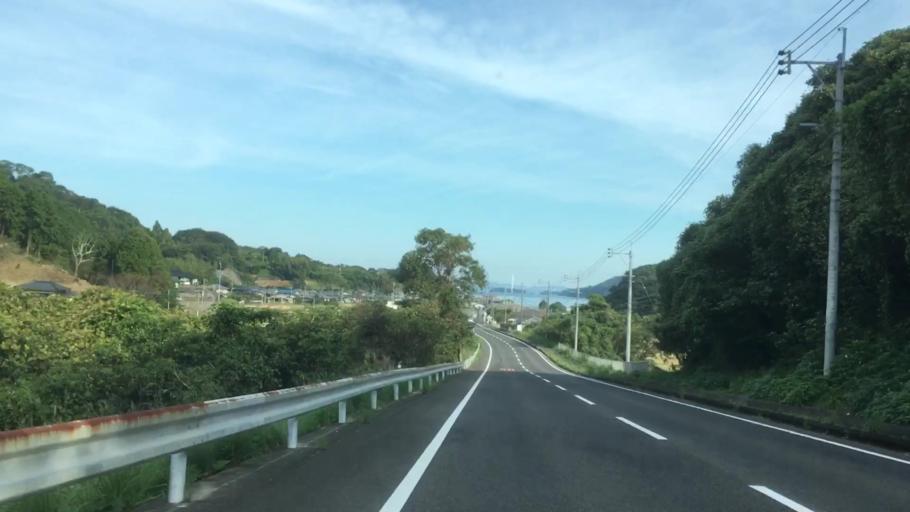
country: JP
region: Nagasaki
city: Sasebo
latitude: 32.9833
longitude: 129.6461
